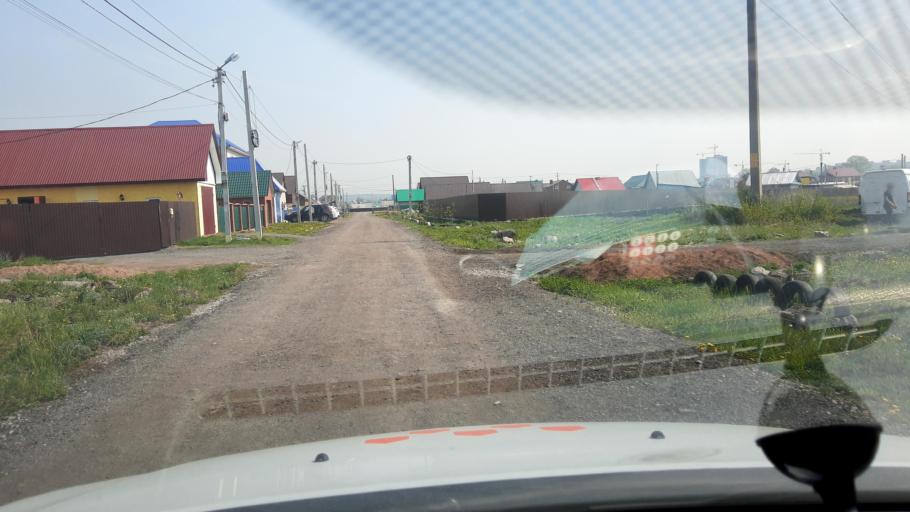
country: RU
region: Bashkortostan
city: Mikhaylovka
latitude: 54.7882
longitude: 55.8223
